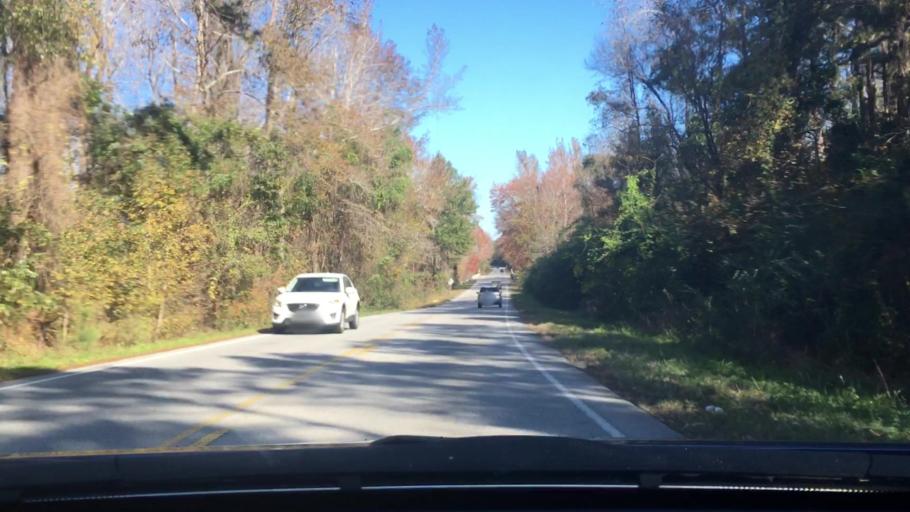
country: US
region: South Carolina
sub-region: Sumter County
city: Lakewood
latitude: 33.8768
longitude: -80.3672
